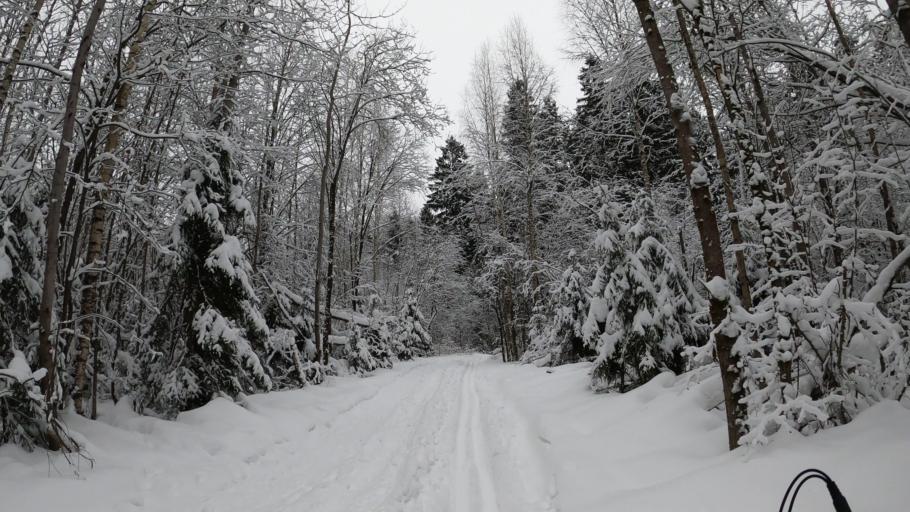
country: RU
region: Moskovskaya
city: Firsanovka
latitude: 55.9530
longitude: 37.2224
